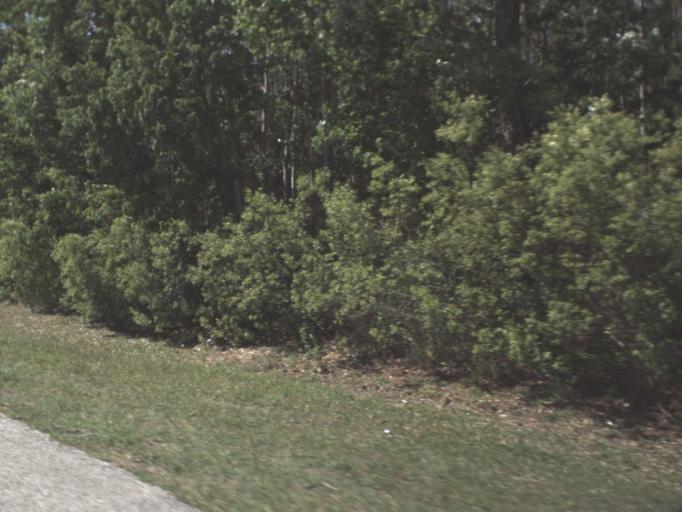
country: US
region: Florida
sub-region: Flagler County
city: Palm Coast
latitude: 29.6368
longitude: -81.2849
